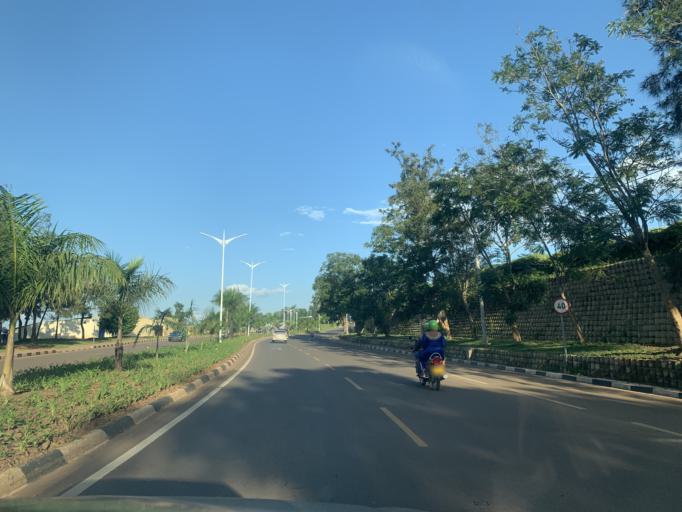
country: RW
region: Kigali
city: Kigali
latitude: -1.9638
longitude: 30.1279
